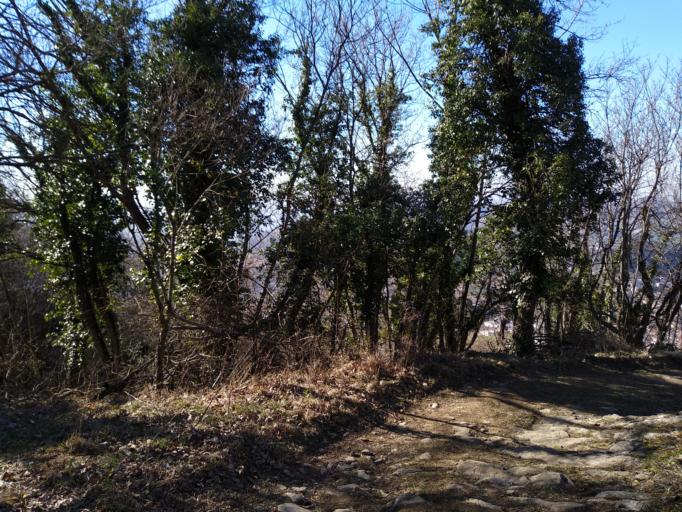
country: IT
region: Emilia-Romagna
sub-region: Provincia di Reggio Emilia
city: Castelnovo ne'Monti
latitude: 44.4240
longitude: 10.4147
